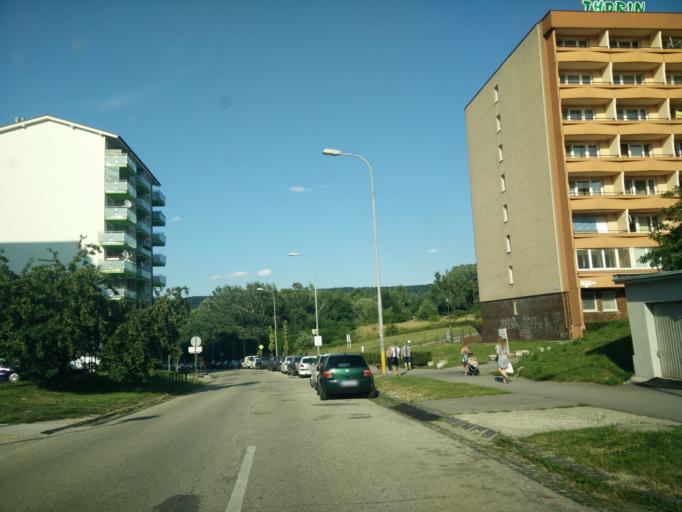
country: AT
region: Lower Austria
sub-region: Politischer Bezirk Bruck an der Leitha
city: Wolfsthal
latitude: 48.1955
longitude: 17.0351
